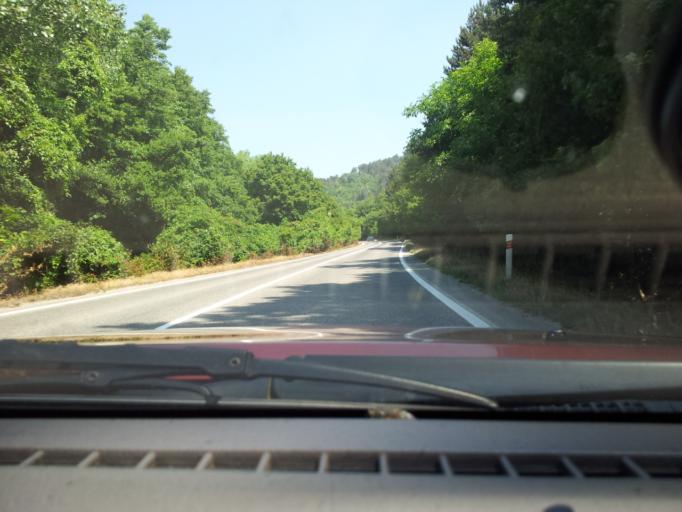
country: SK
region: Trnavsky
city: Smolenice
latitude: 48.5388
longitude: 17.4511
